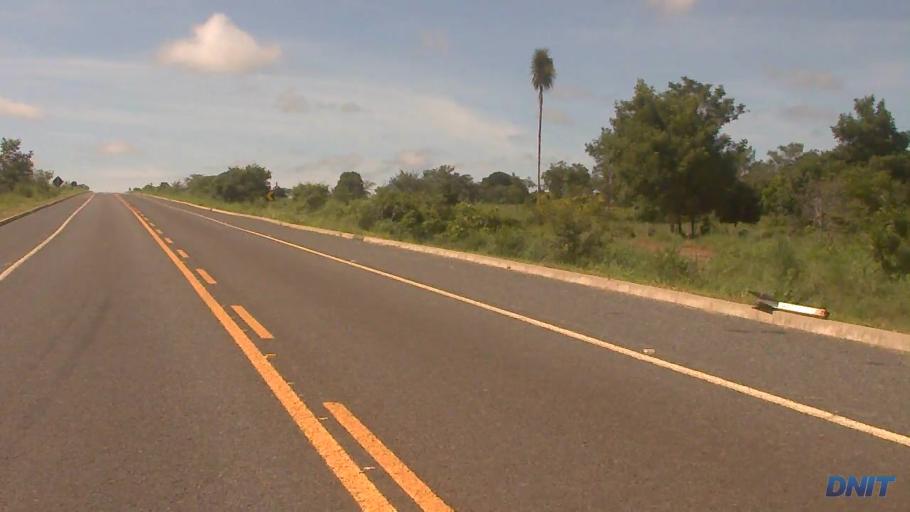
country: BR
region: Goias
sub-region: Sao Miguel Do Araguaia
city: Sao Miguel do Araguaia
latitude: -13.2966
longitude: -50.1764
